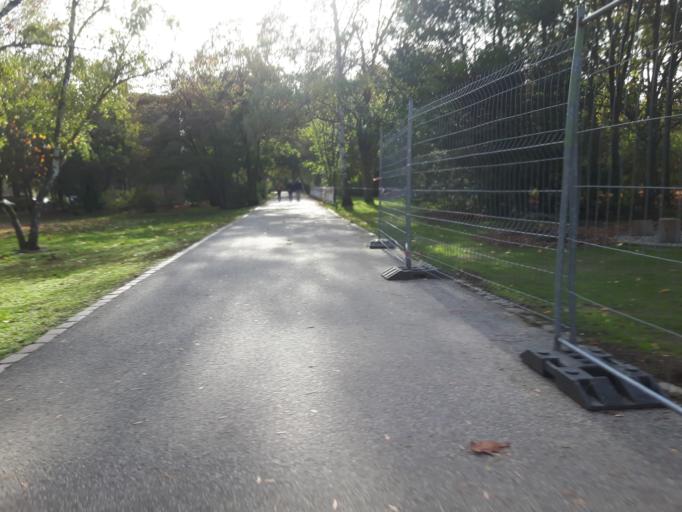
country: DE
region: Berlin
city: Spandau
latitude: 52.5405
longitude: 13.1930
